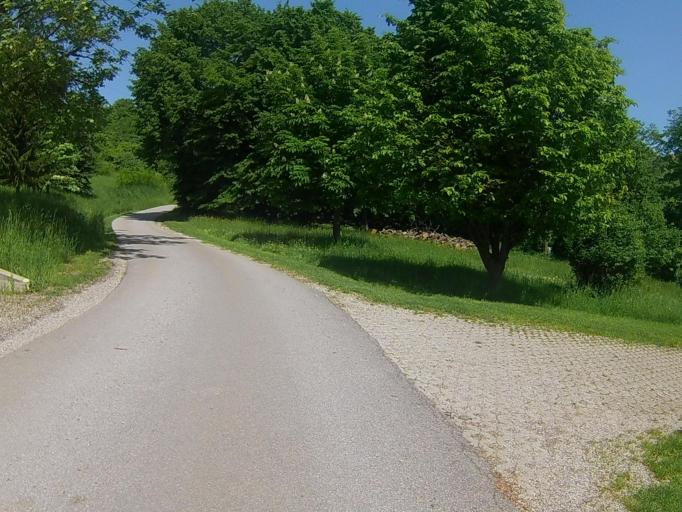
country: SI
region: Pesnica
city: Pesnica pri Mariboru
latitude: 46.5663
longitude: 15.7049
